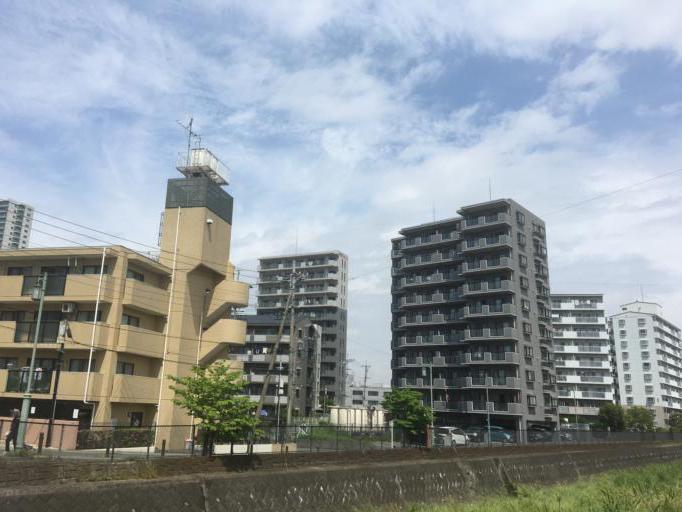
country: JP
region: Saitama
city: Shimotoda
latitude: 35.8416
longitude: 139.6513
